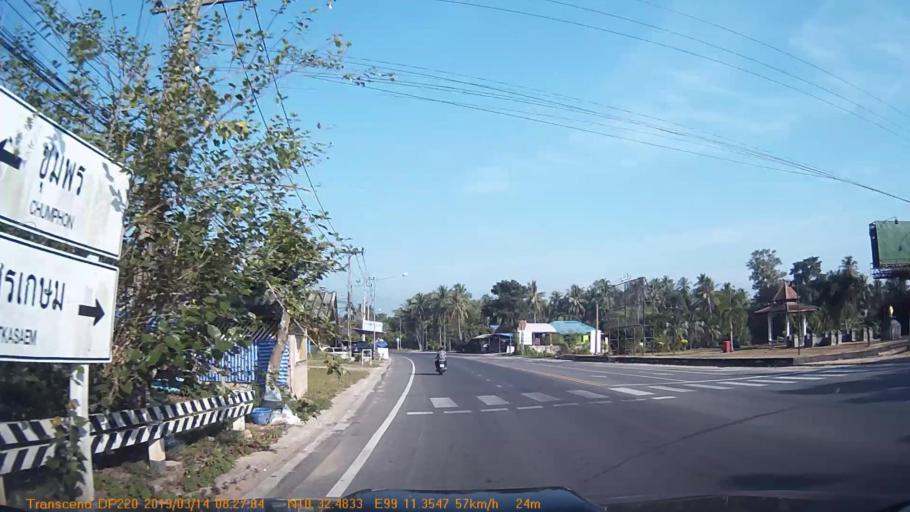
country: TH
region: Chumphon
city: Chumphon
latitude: 10.5416
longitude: 99.1891
